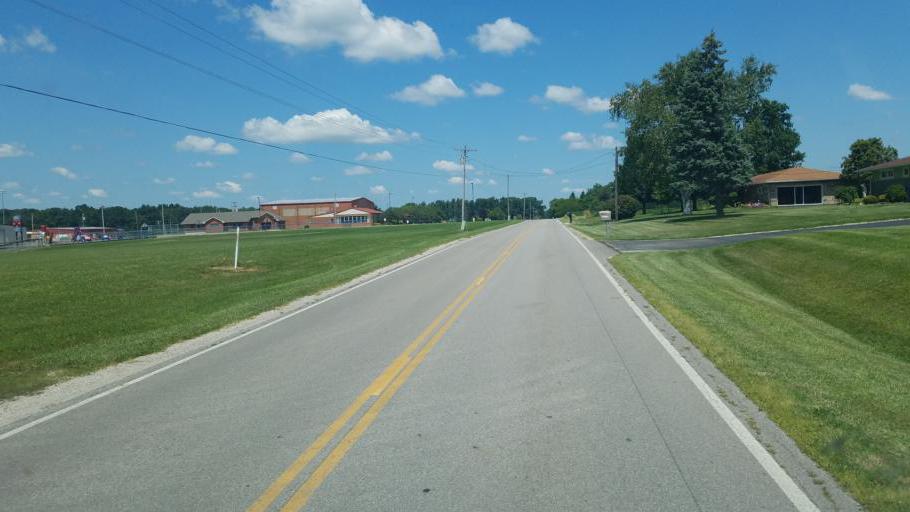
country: US
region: Ohio
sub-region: Marion County
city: Marion
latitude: 40.6458
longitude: -83.1733
